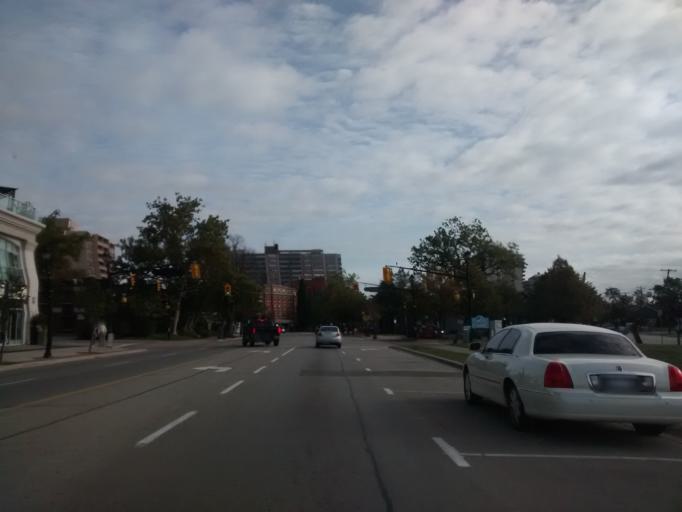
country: CA
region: Ontario
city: Burlington
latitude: 43.3254
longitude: -79.7941
